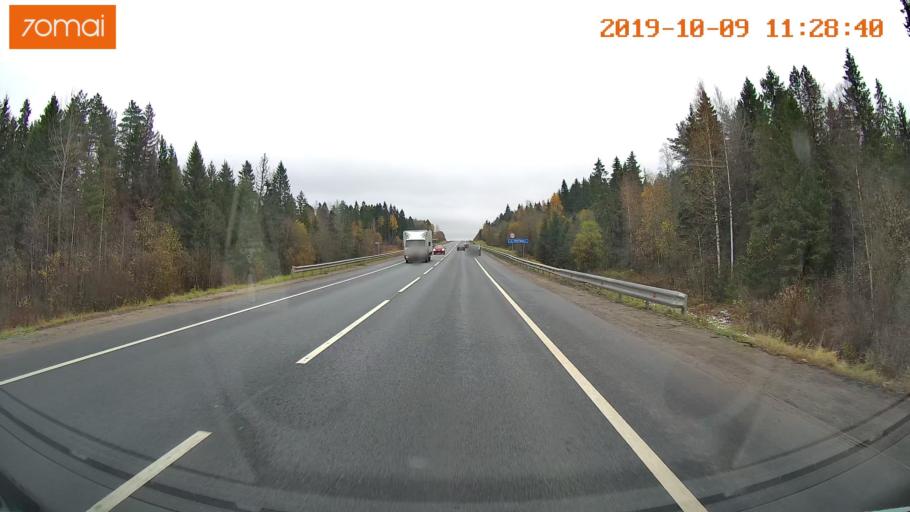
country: RU
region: Vologda
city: Vologda
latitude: 59.0666
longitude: 40.0419
